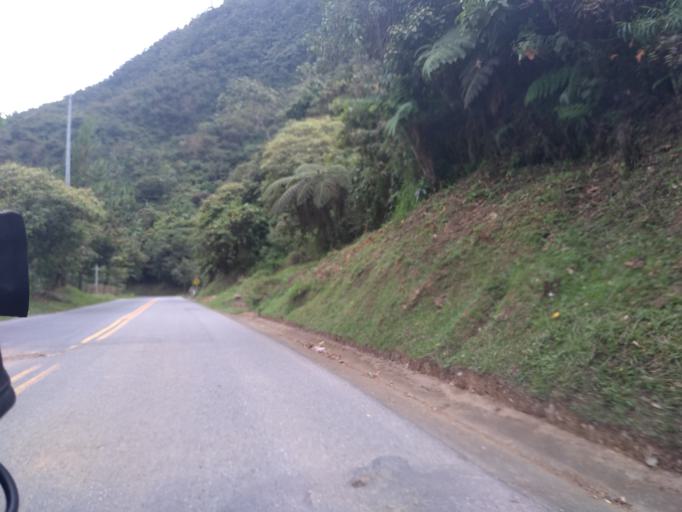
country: CO
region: Cauca
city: Rosas
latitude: 2.2600
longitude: -76.7531
